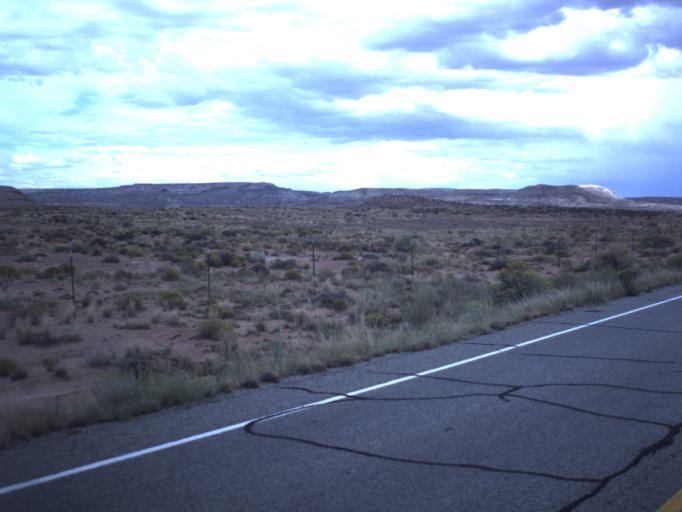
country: US
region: Utah
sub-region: San Juan County
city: Blanding
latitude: 37.2917
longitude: -109.4177
